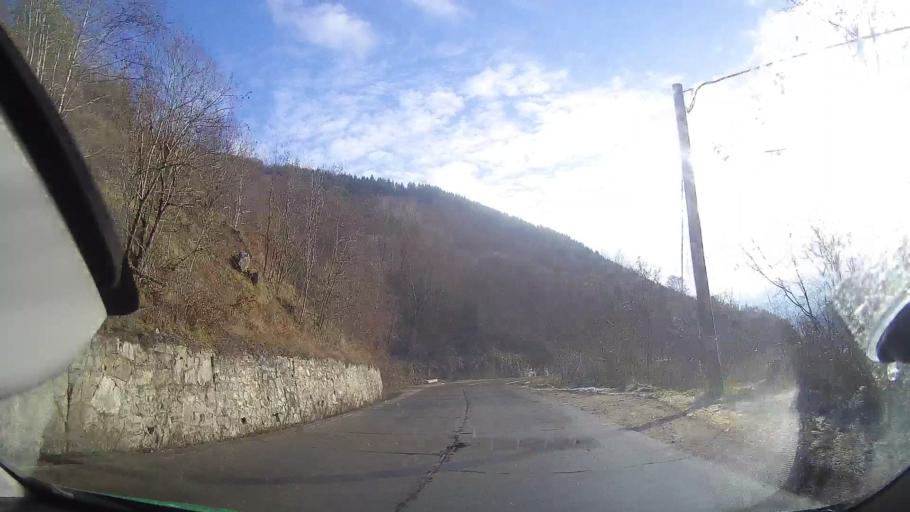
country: RO
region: Alba
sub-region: Comuna Sohodol
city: Sohodol
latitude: 46.3799
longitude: 23.0125
